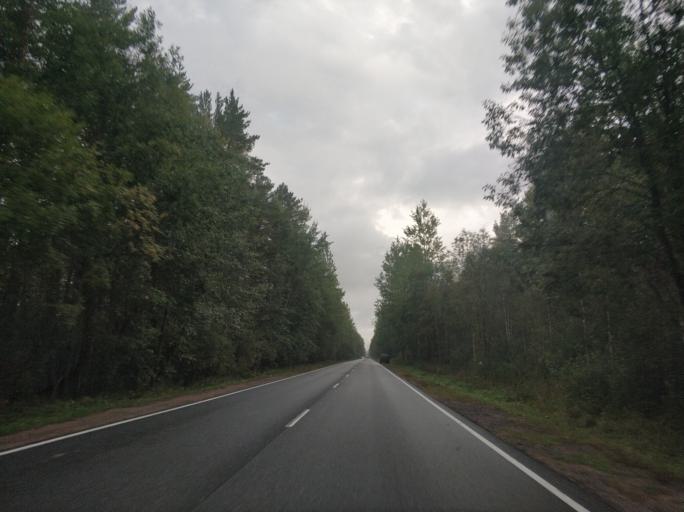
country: RU
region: Leningrad
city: Borisova Griva
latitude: 60.1457
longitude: 30.9444
